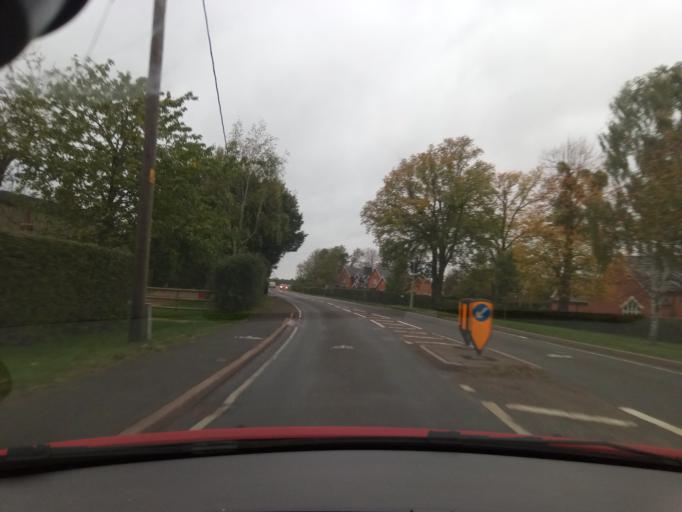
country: GB
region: England
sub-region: Essex
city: Great Yeldham
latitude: 52.0411
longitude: 0.5305
